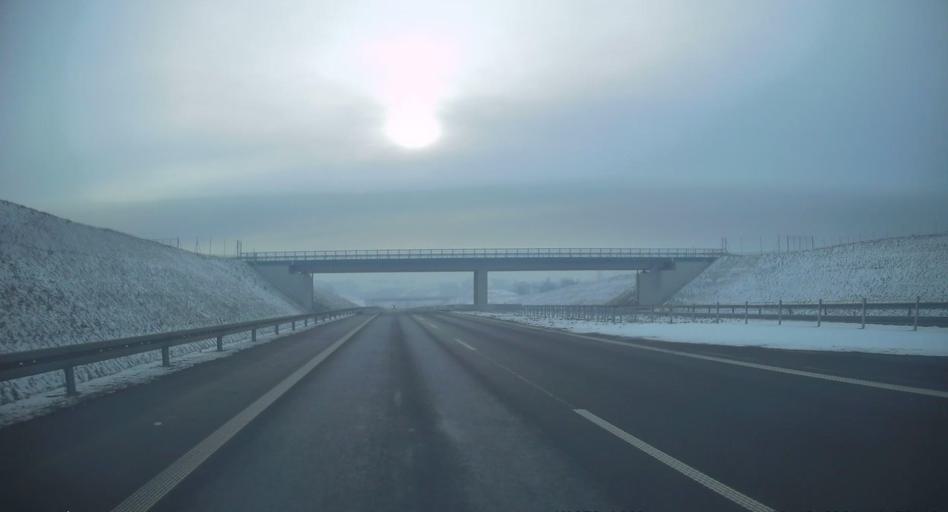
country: PL
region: Lesser Poland Voivodeship
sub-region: Powiat krakowski
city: Slomniki
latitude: 50.2689
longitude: 20.0205
